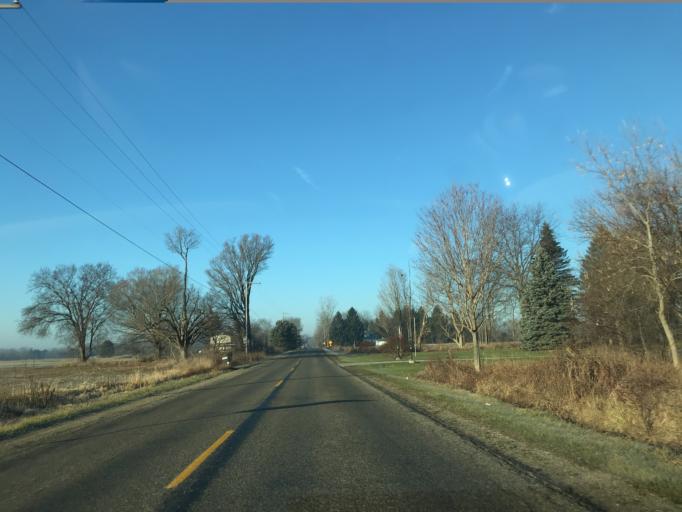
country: US
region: Michigan
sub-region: Eaton County
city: Dimondale
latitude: 42.6620
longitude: -84.6308
